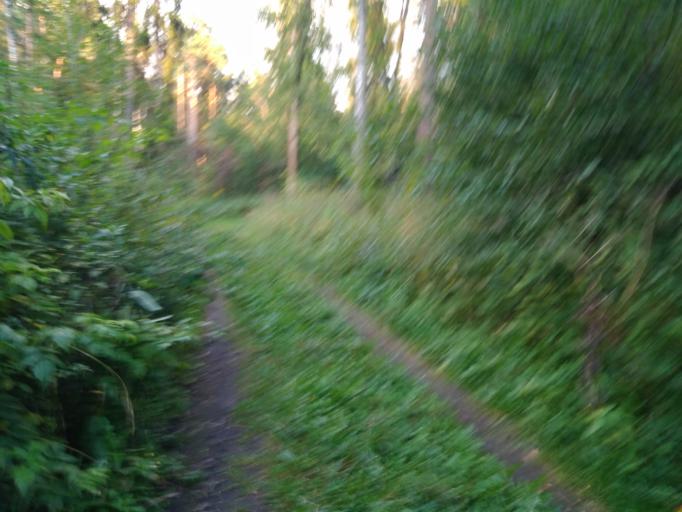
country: RU
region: Moskovskaya
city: Zhukovskiy
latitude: 55.5804
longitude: 38.1154
